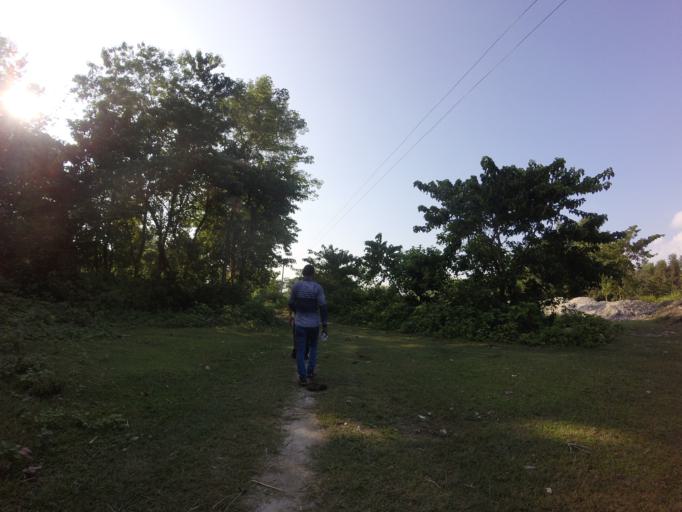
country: NP
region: Far Western
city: Tikapur
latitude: 28.4451
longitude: 81.0773
